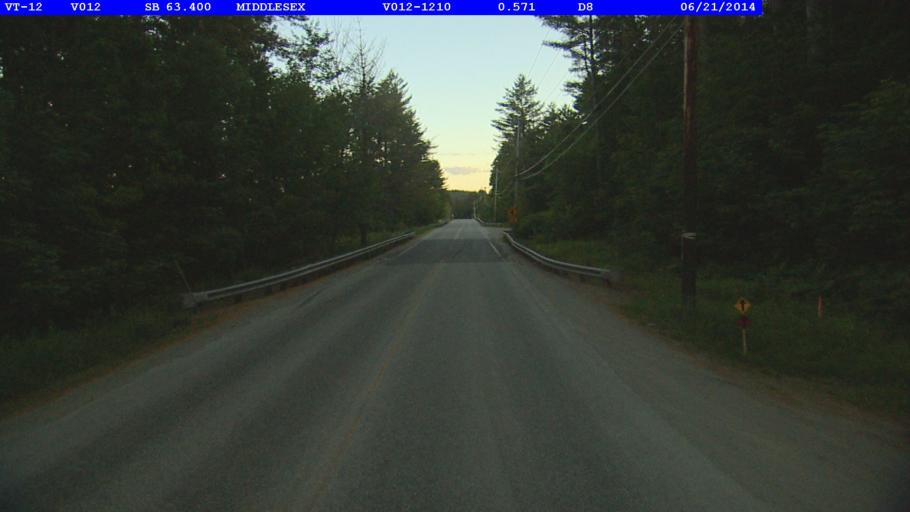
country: US
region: Vermont
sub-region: Washington County
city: Montpelier
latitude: 44.3132
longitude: -72.5781
